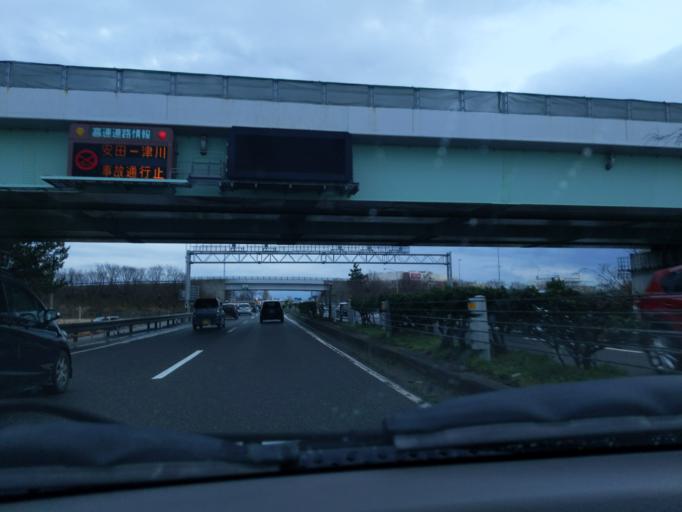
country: JP
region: Niigata
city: Kameda-honcho
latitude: 37.8810
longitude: 139.0815
